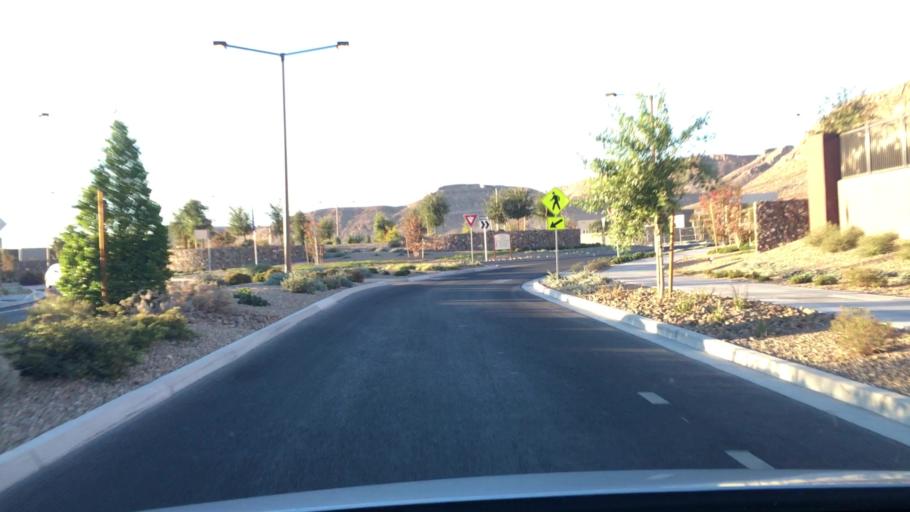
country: US
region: Nevada
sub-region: Clark County
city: Summerlin South
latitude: 36.0757
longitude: -115.3188
